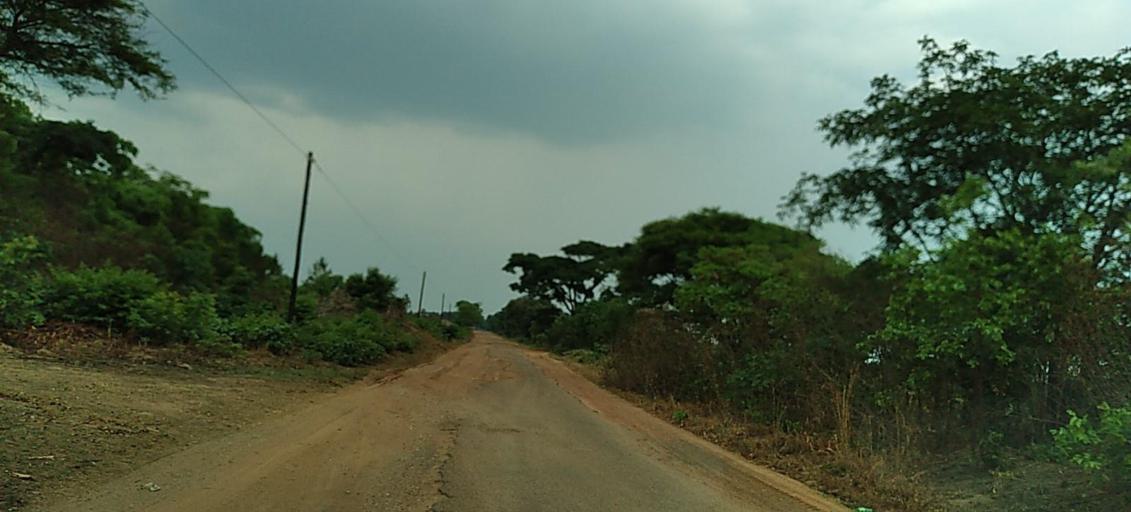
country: ZM
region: Copperbelt
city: Kalulushi
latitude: -12.8865
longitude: 28.1191
